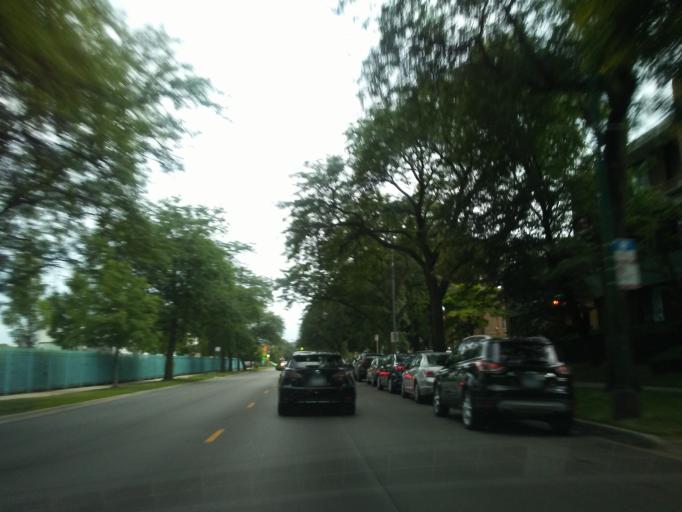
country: US
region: Illinois
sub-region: Cook County
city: Evanston
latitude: 41.9996
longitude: -87.6776
